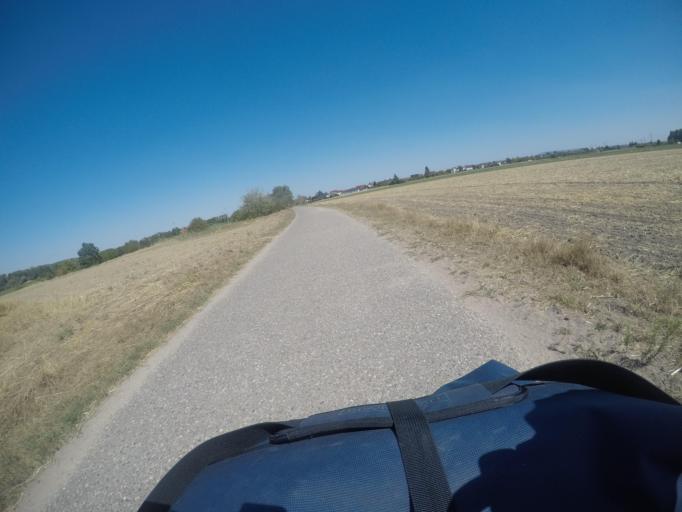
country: DE
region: Baden-Wuerttemberg
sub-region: Karlsruhe Region
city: Philippsburg
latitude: 49.2490
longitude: 8.4806
